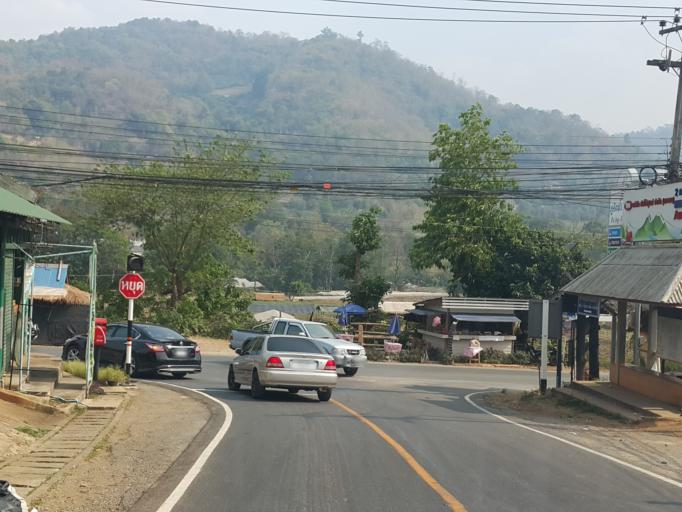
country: TH
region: Chiang Mai
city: Samoeng
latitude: 18.8936
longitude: 98.8342
